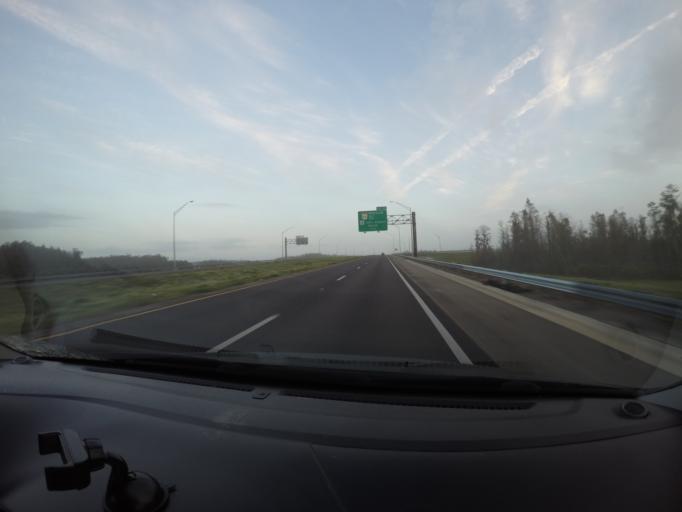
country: US
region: Florida
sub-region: Orange County
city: Conway
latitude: 28.4242
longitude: -81.2277
